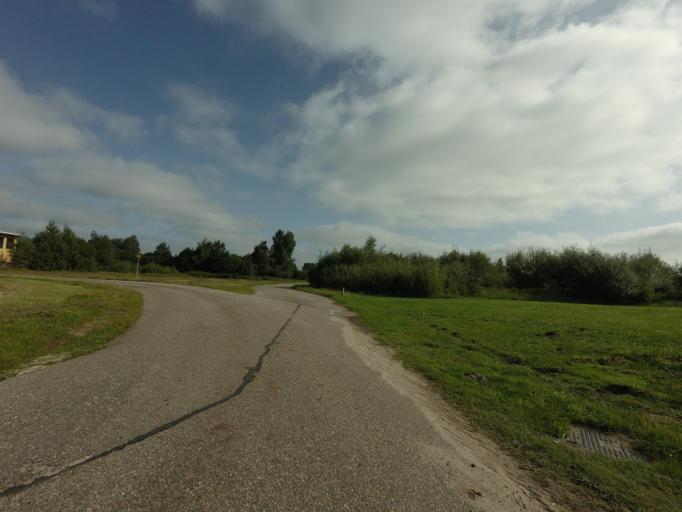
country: NL
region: Overijssel
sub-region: Gemeente Steenwijkerland
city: Steenwijk
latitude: 52.8043
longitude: 6.1378
